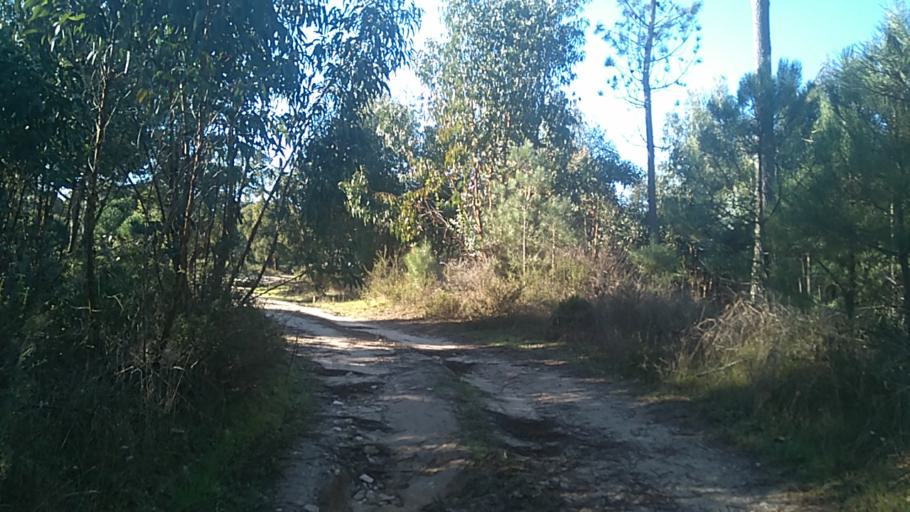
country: PT
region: Santarem
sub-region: Coruche
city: Coruche
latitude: 38.8651
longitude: -8.5185
